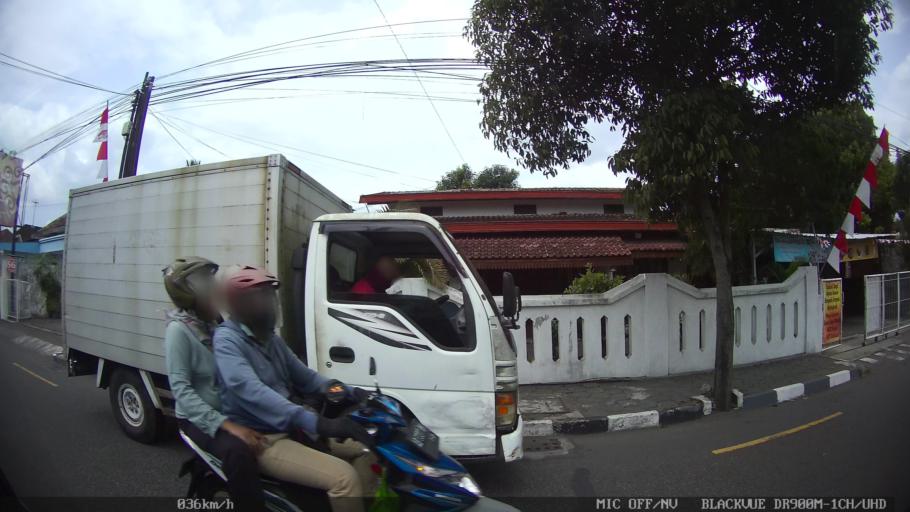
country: ID
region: Daerah Istimewa Yogyakarta
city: Yogyakarta
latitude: -7.7972
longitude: 110.3759
